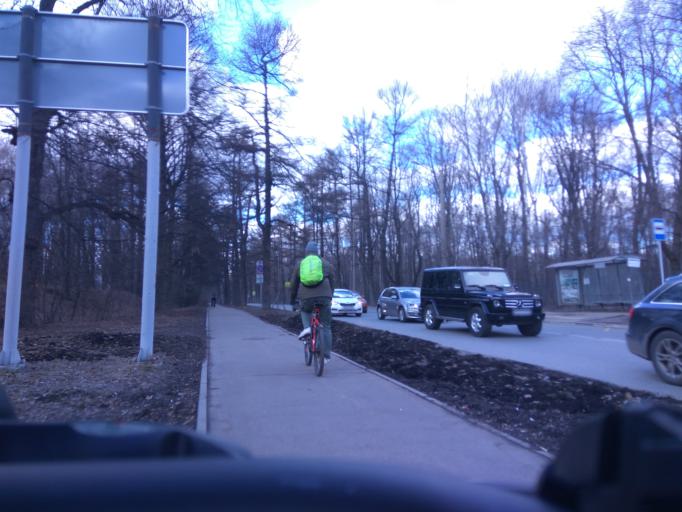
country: RU
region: Moscow
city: Sokol'niki
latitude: 55.7928
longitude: 37.6589
